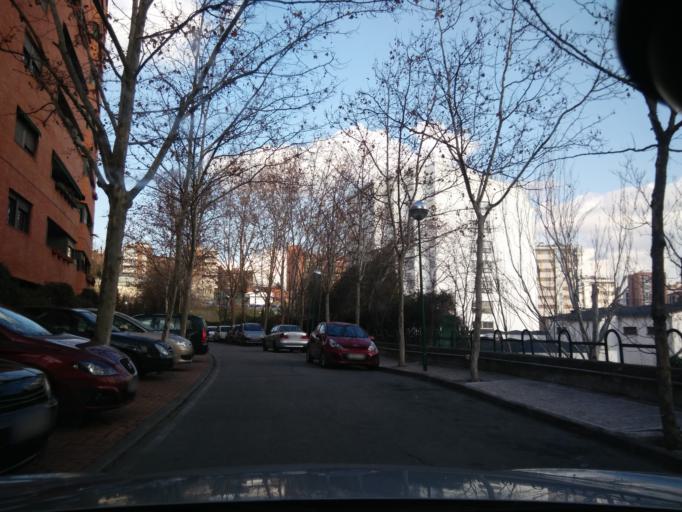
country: ES
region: Madrid
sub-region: Provincia de Madrid
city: Tetuan de las Victorias
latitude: 40.4512
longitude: -3.7159
